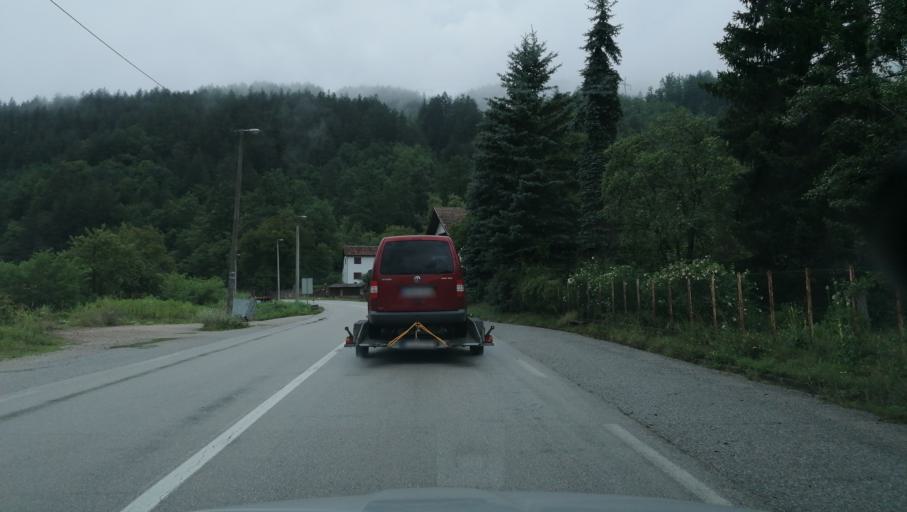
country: BA
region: Republika Srpska
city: Visegrad
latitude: 43.7824
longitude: 19.3565
